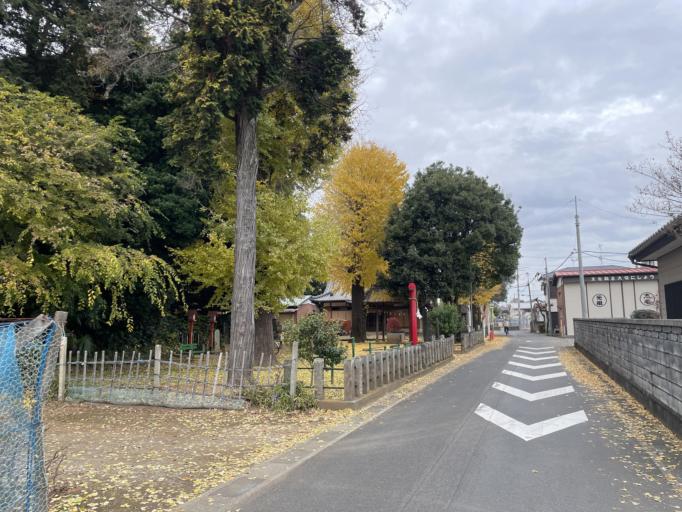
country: JP
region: Saitama
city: Shiraoka
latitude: 36.0284
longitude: 139.6559
